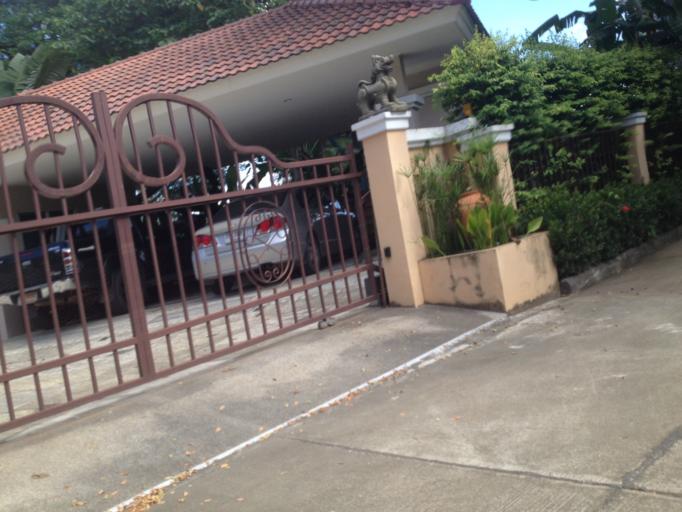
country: TH
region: Chiang Mai
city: Hang Dong
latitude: 18.7076
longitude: 98.9108
